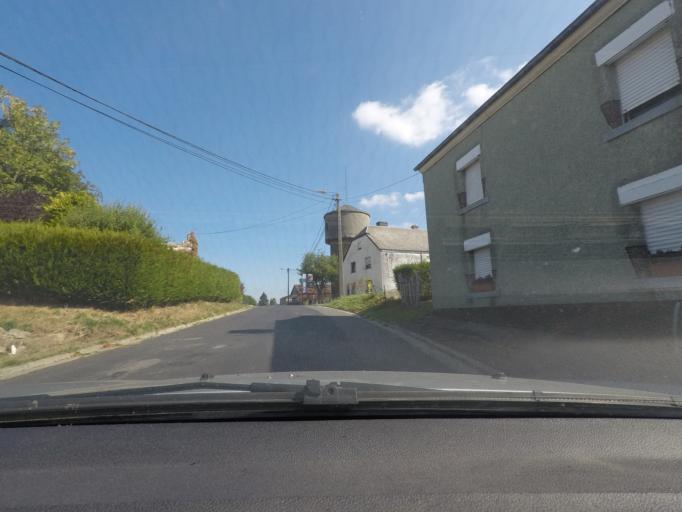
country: BE
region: Wallonia
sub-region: Province du Luxembourg
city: Fauvillers
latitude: 49.7930
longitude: 5.6282
